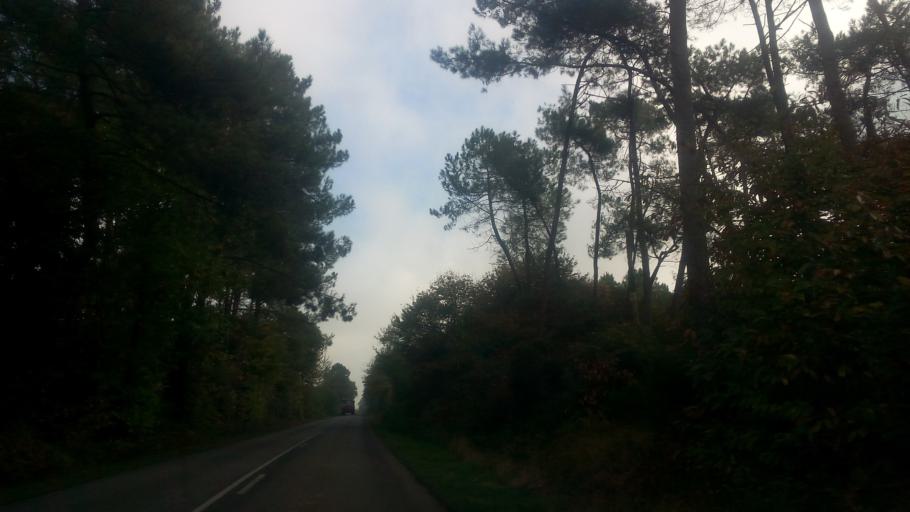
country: FR
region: Pays de la Loire
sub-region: Departement de la Loire-Atlantique
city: Guemene-Penfao
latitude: 47.6292
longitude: -1.8089
